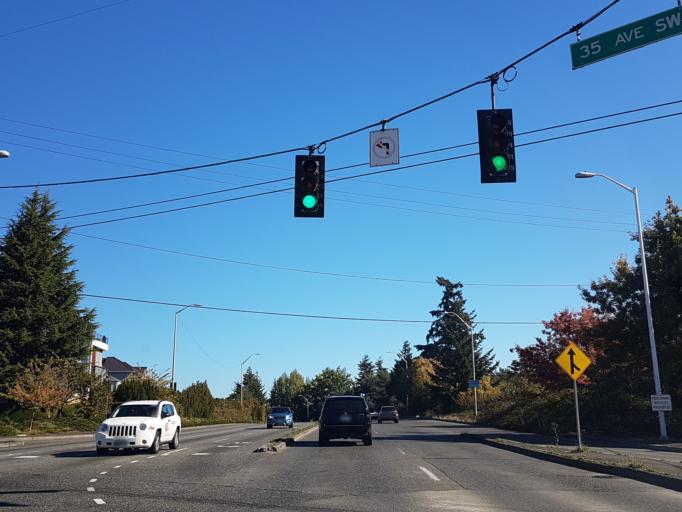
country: US
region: Washington
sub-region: King County
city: White Center
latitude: 47.5650
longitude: -122.3763
